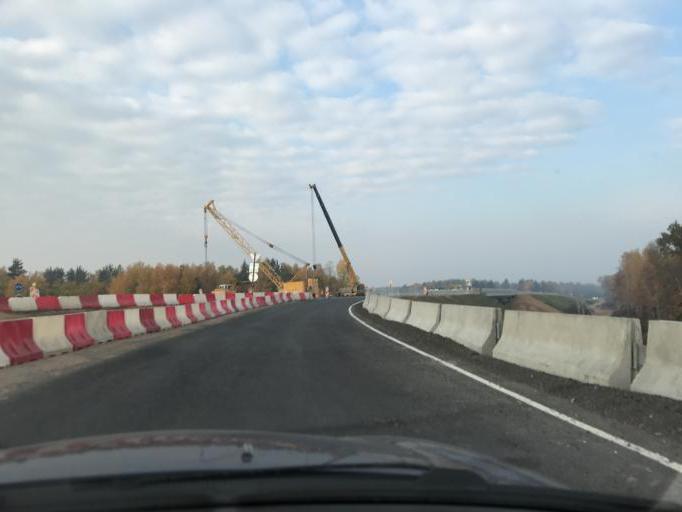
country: BY
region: Grodnenskaya
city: Lida
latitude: 53.8301
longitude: 25.3481
